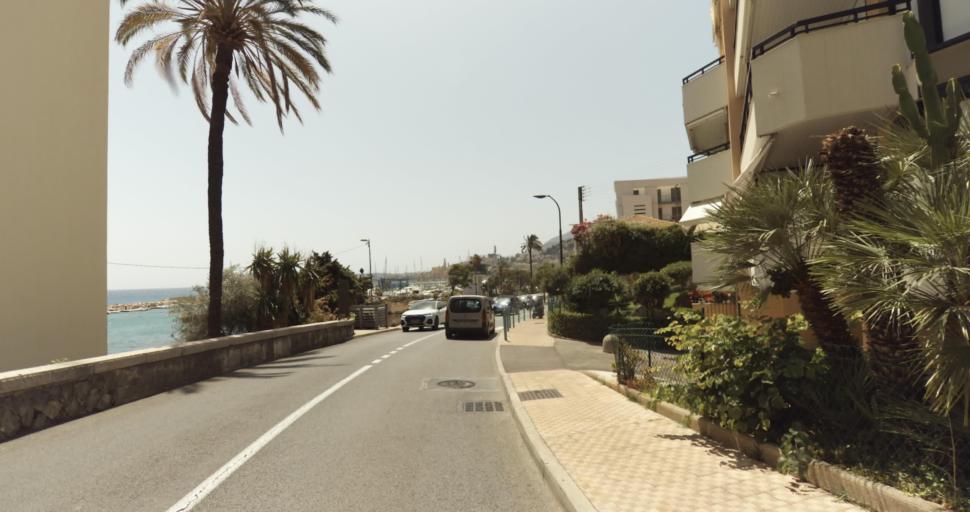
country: FR
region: Provence-Alpes-Cote d'Azur
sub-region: Departement des Alpes-Maritimes
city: Menton
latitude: 43.7852
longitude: 7.5228
